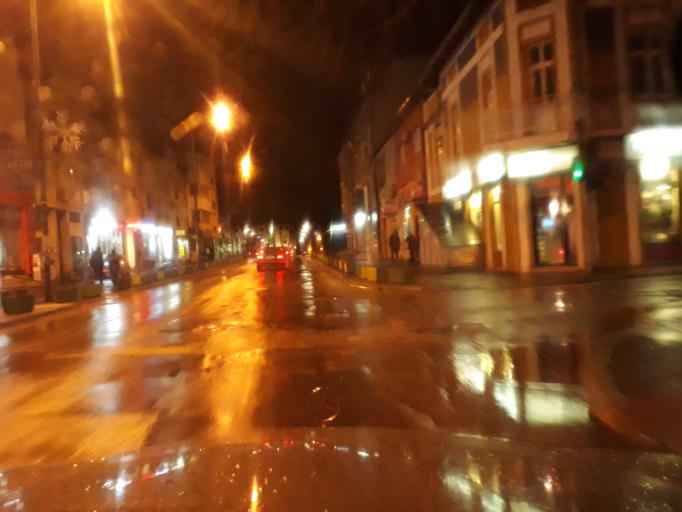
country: BA
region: Federation of Bosnia and Herzegovina
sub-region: Kanton Sarajevo
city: Sarajevo
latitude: 43.8309
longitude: 18.3064
